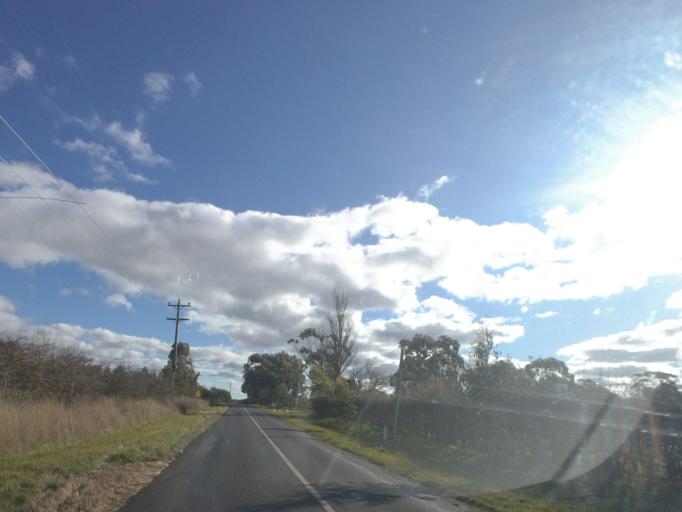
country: AU
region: Victoria
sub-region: Mount Alexander
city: Castlemaine
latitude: -37.2526
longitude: 144.4134
